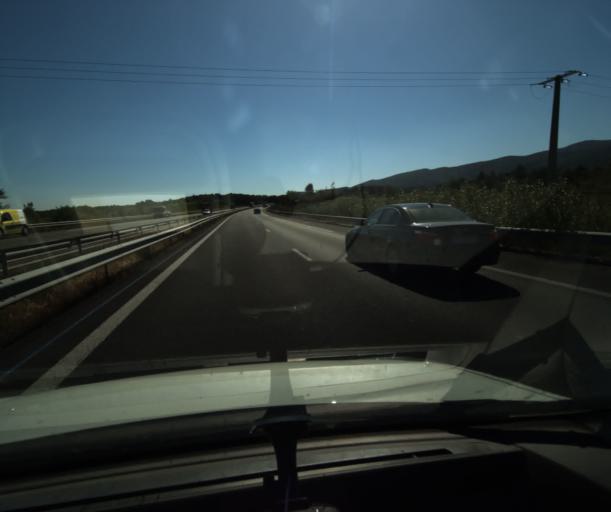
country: FR
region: Languedoc-Roussillon
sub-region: Departement de l'Aude
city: Capendu
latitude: 43.1789
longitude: 2.5809
